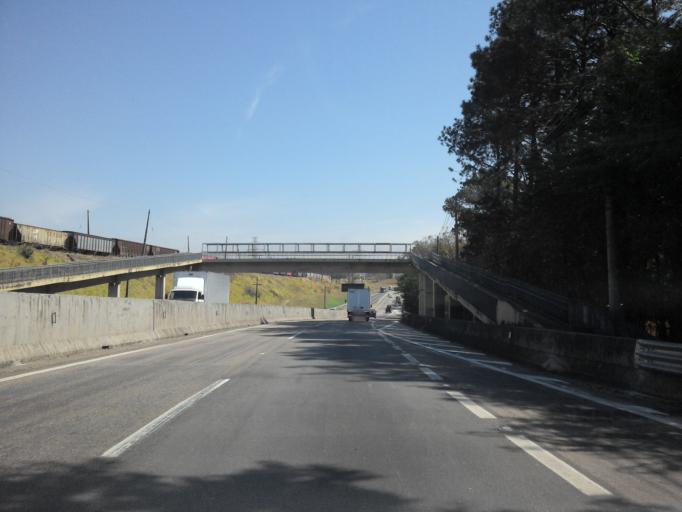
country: BR
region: Sao Paulo
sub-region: Campinas
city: Campinas
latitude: -22.8987
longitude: -47.1189
